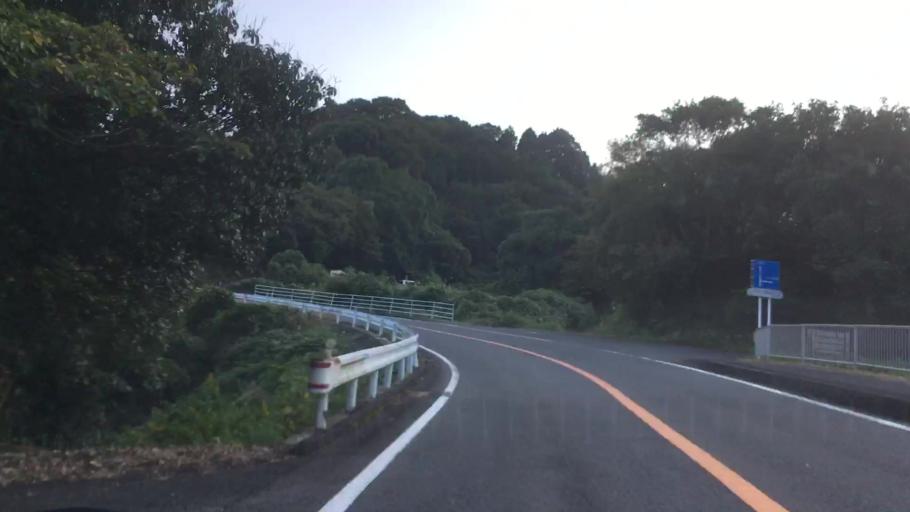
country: JP
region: Nagasaki
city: Sasebo
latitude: 32.9949
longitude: 129.7242
